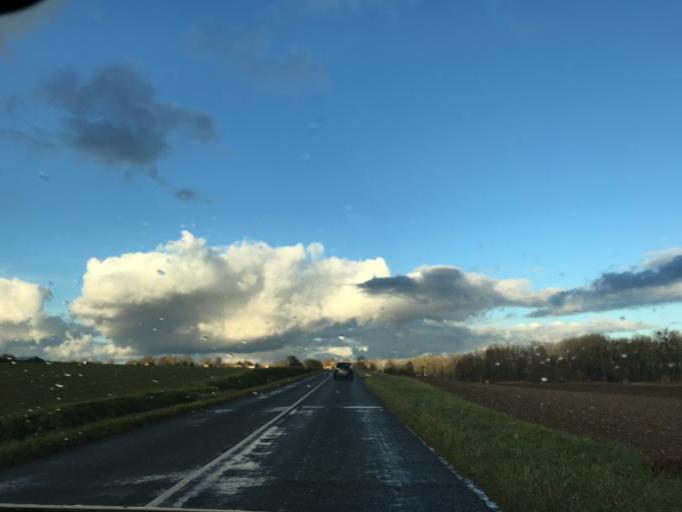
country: FR
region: Ile-de-France
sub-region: Departement de Seine-et-Marne
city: Juilly
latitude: 48.9954
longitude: 2.7002
